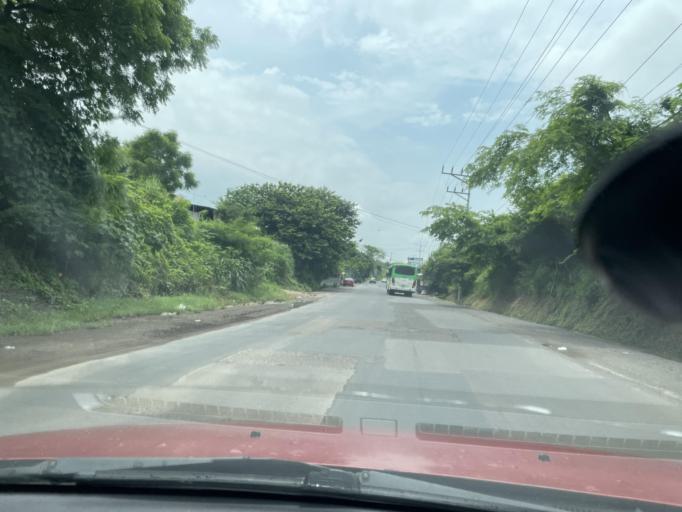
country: SV
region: La Union
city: Santa Rosa de Lima
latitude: 13.6192
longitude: -87.8601
